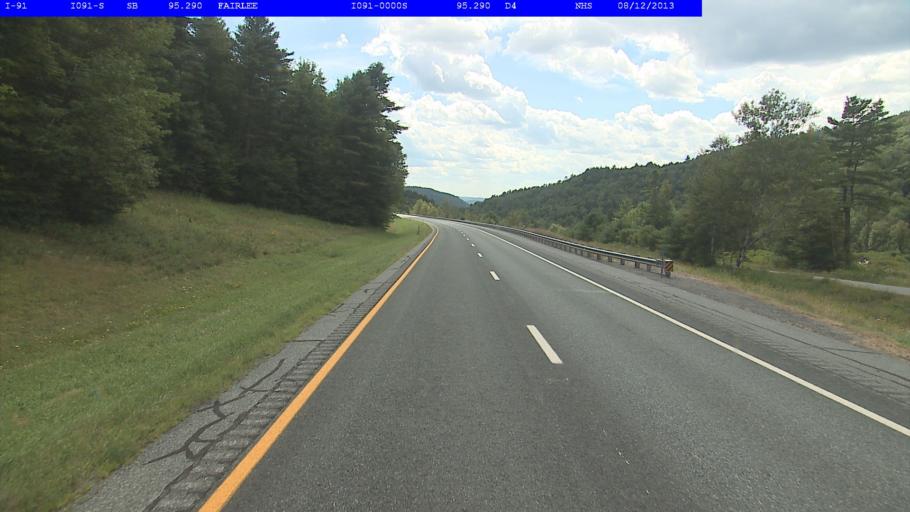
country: US
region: New Hampshire
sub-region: Grafton County
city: Orford
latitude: 43.9518
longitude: -72.1322
